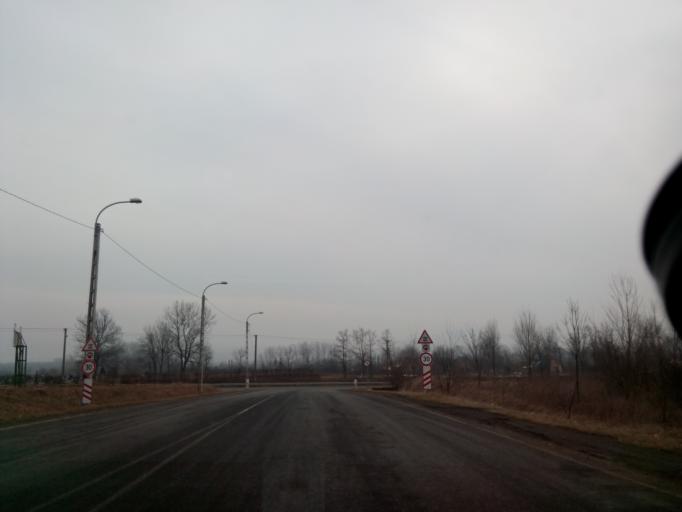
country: HU
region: Borsod-Abauj-Zemplen
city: Gonc
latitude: 48.5266
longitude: 21.2536
